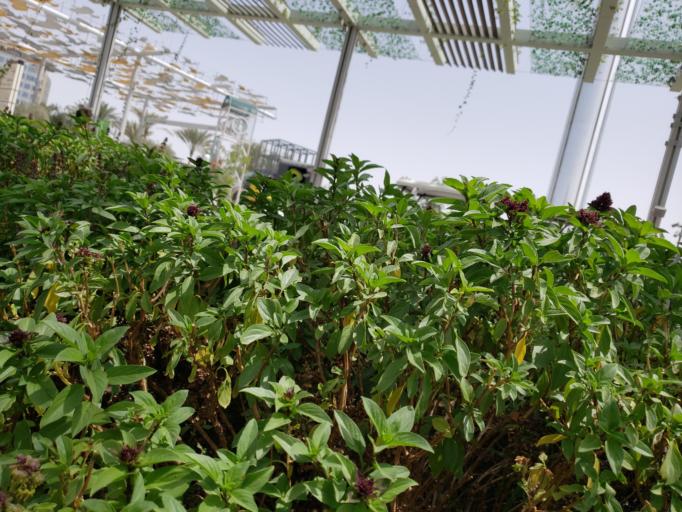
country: AE
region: Dubai
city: Dubai
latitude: 24.9580
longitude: 55.1500
